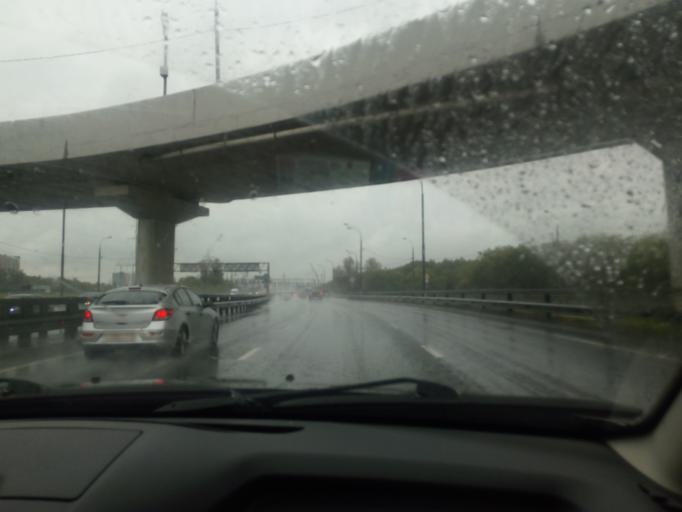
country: RU
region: Moscow
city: Zhulebino
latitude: 55.7078
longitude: 37.8569
